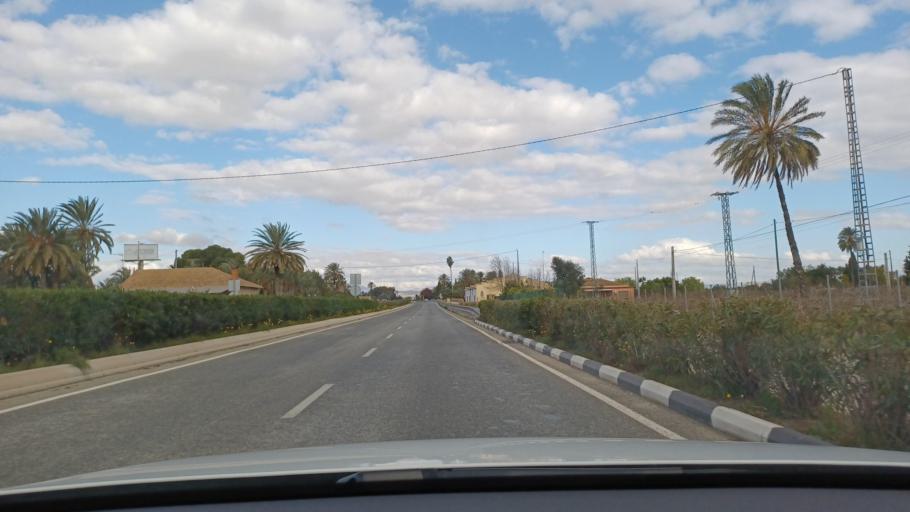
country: ES
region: Valencia
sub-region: Provincia de Alicante
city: Elche
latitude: 38.1962
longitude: -0.7005
